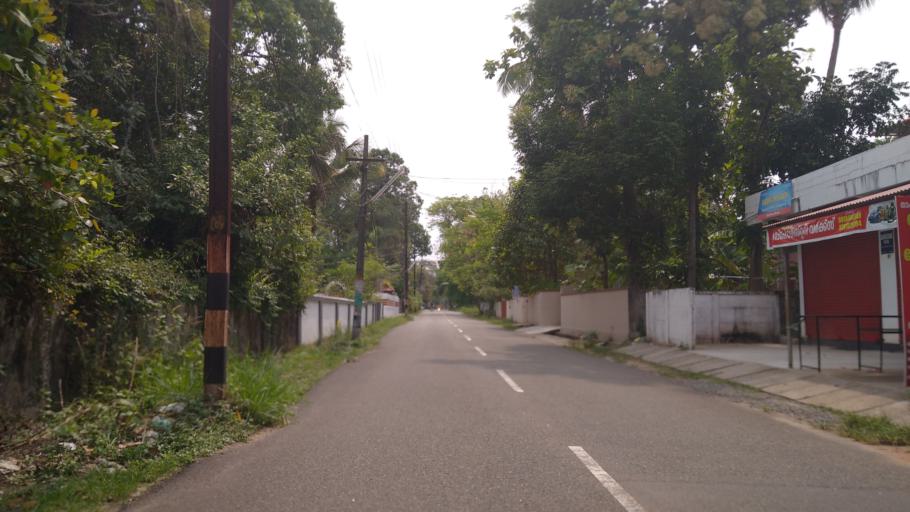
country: IN
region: Kerala
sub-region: Ernakulam
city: Elur
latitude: 10.1455
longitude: 76.2487
